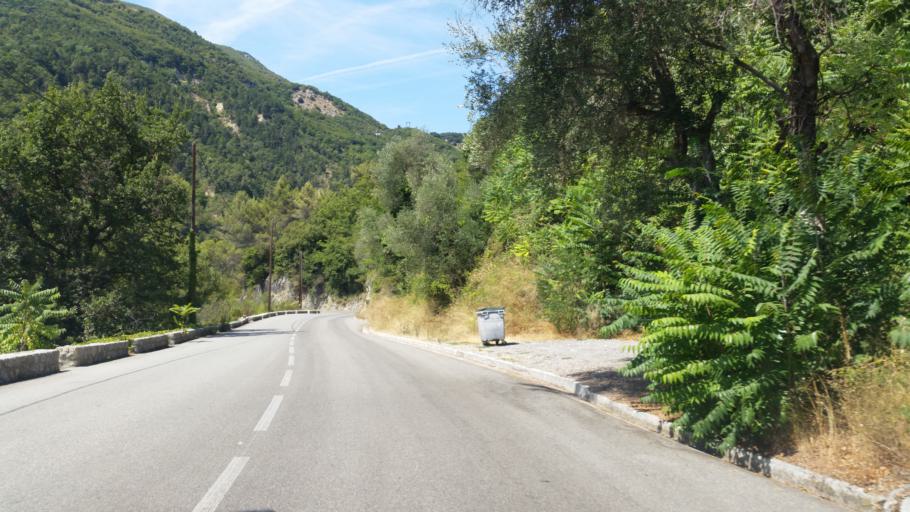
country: FR
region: Provence-Alpes-Cote d'Azur
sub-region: Departement des Alpes-Maritimes
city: Sainte-Agnes
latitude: 43.8290
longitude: 7.4804
